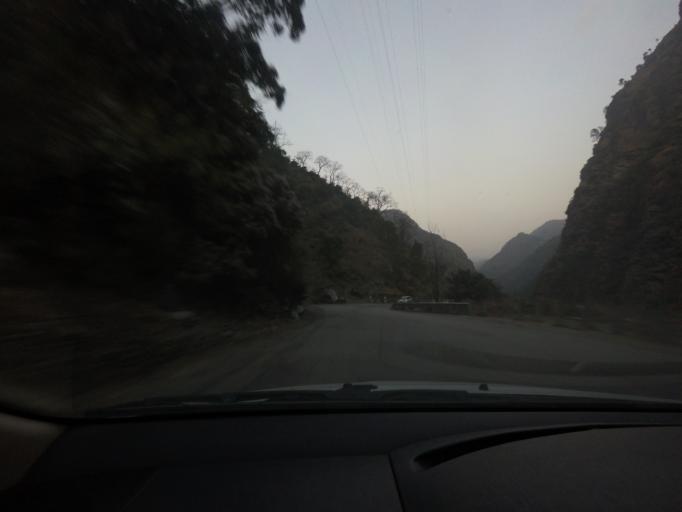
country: IN
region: Himachal Pradesh
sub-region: Mandi
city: Pandoh
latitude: 31.6940
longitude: 77.1368
